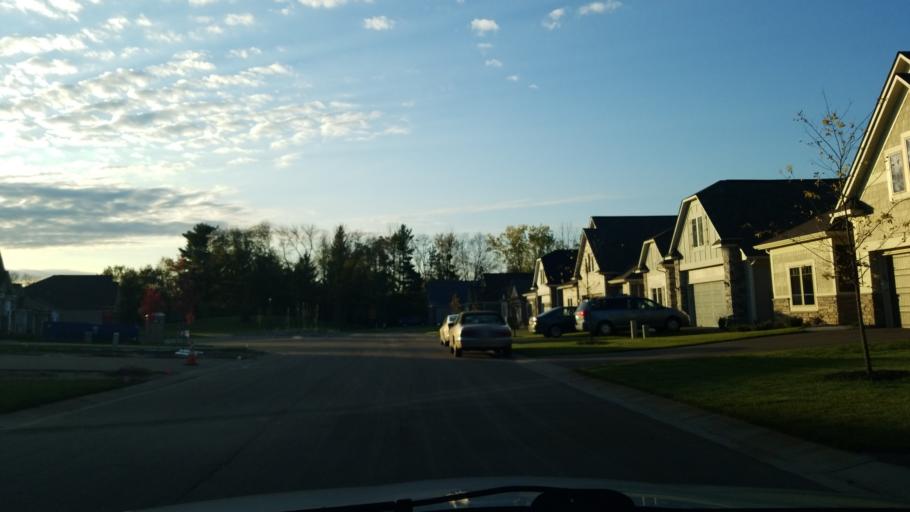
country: US
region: Wisconsin
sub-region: Saint Croix County
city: Hudson
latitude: 44.9677
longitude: -92.7294
